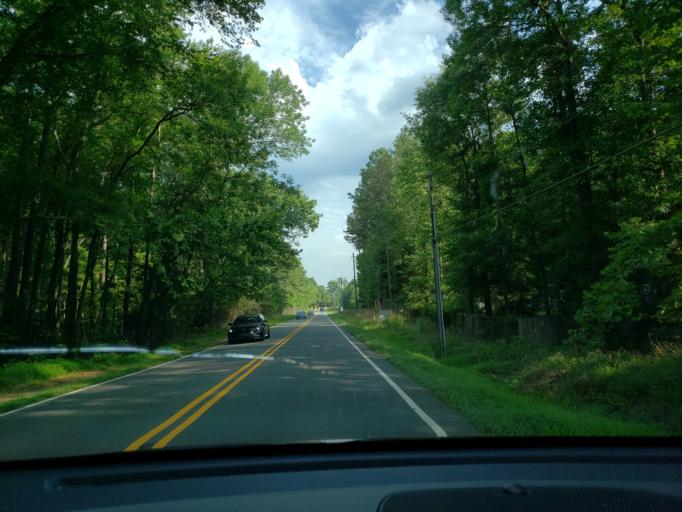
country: US
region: North Carolina
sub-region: Orange County
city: Chapel Hill
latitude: 35.9017
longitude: -78.9814
